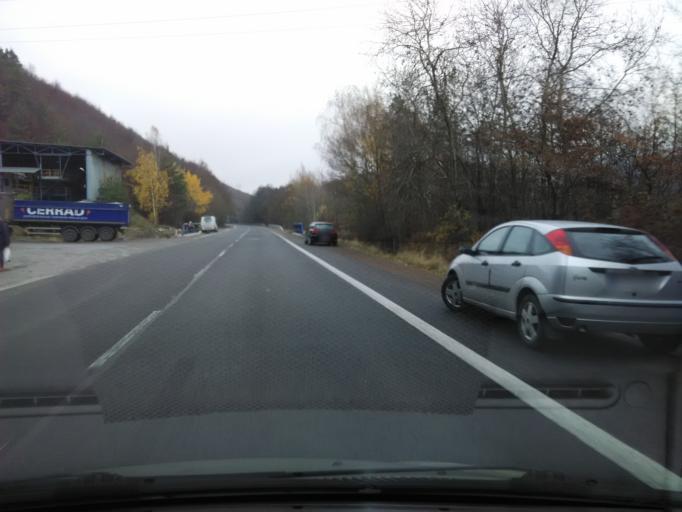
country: SK
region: Banskobystricky
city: Ziar nad Hronom
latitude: 48.6228
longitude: 18.8970
